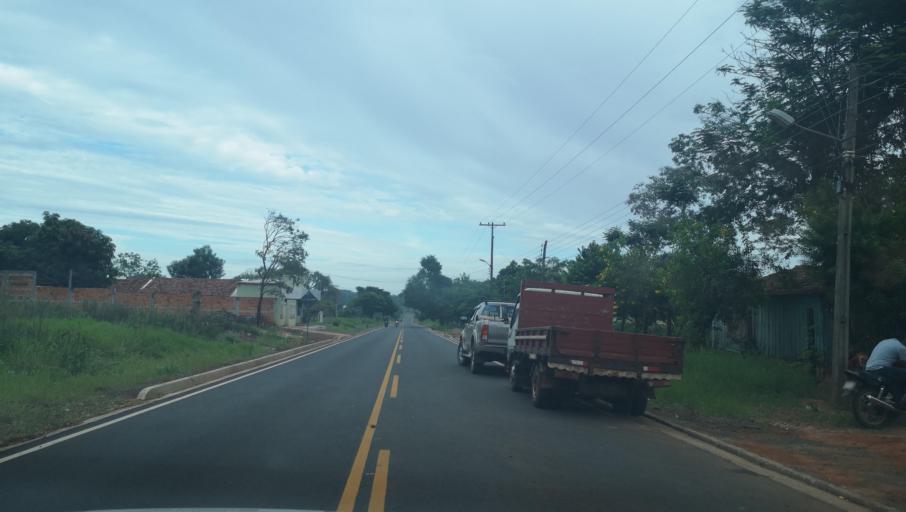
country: PY
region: San Pedro
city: Capiibary
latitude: -24.7450
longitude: -56.0279
